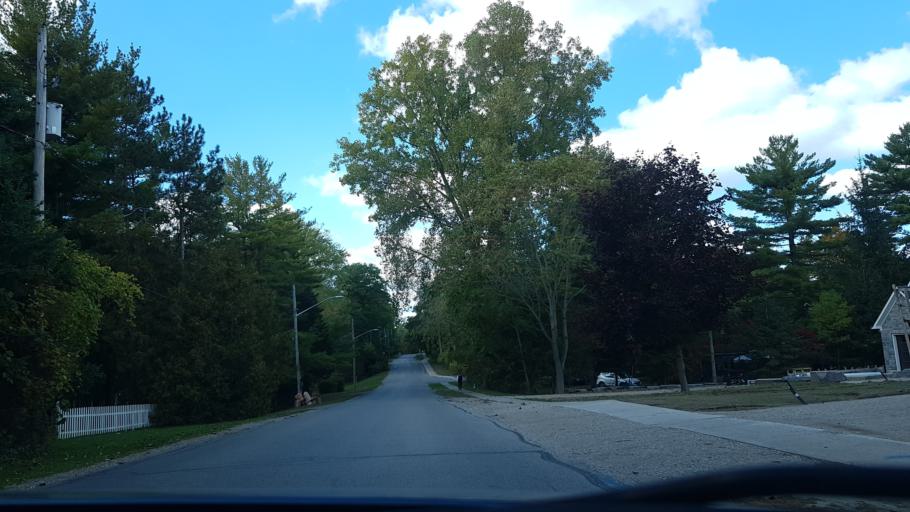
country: CA
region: Ontario
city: Lambton Shores
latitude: 43.3098
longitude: -81.7611
